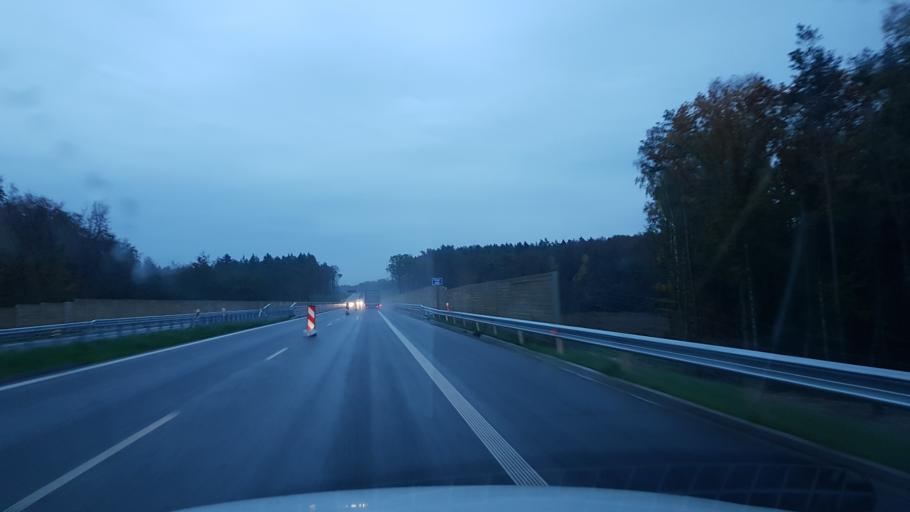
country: PL
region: West Pomeranian Voivodeship
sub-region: Powiat gryficki
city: Ploty
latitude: 53.8255
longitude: 15.2722
